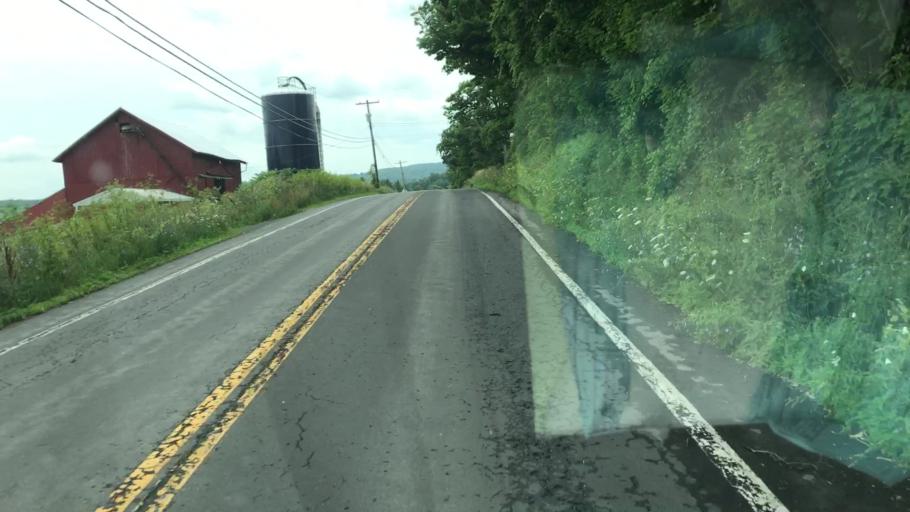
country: US
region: New York
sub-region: Onondaga County
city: Manlius
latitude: 42.9610
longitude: -75.9867
